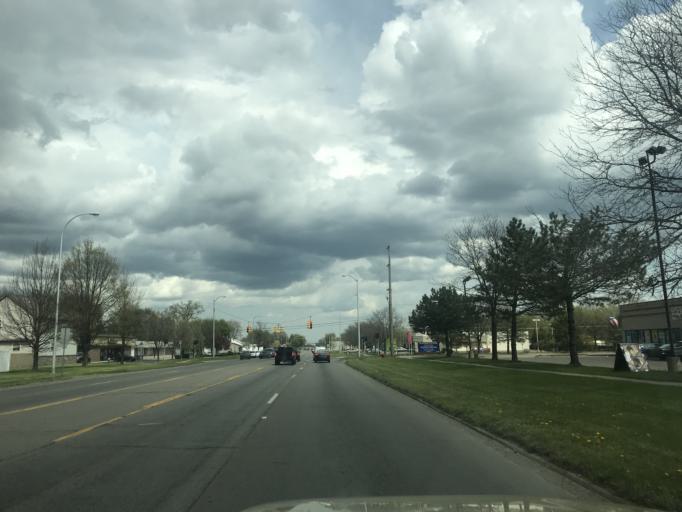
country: US
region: Michigan
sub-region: Wayne County
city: Taylor
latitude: 42.1968
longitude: -83.2933
